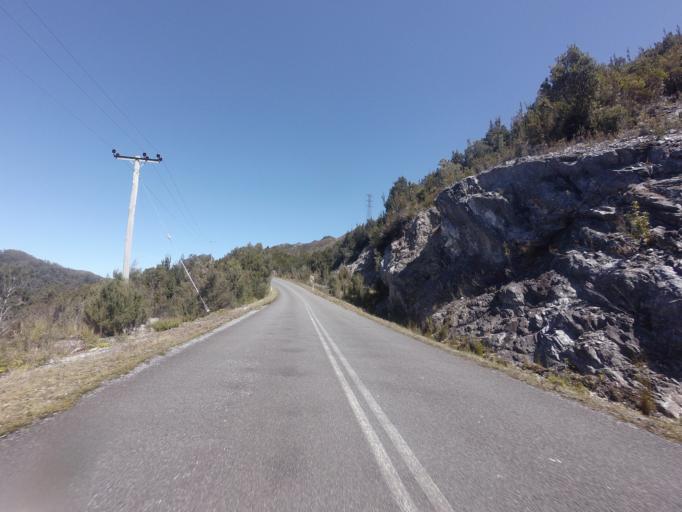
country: AU
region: Tasmania
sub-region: West Coast
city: Queenstown
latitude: -42.7422
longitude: 145.9808
